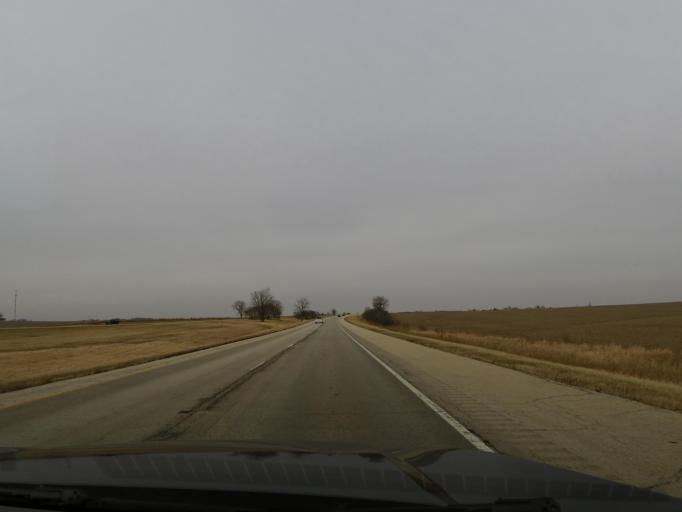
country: US
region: Illinois
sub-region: Knox County
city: Galesburg
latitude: 41.1384
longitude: -90.3323
